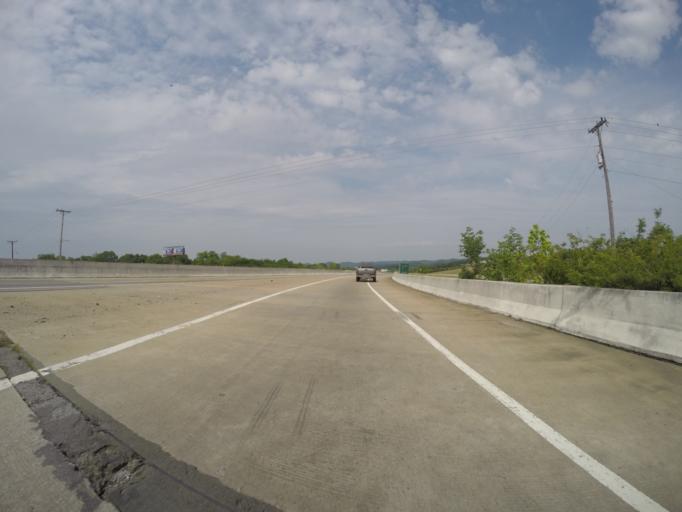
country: US
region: Tennessee
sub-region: Davidson County
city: Nashville
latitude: 36.2416
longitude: -86.7565
